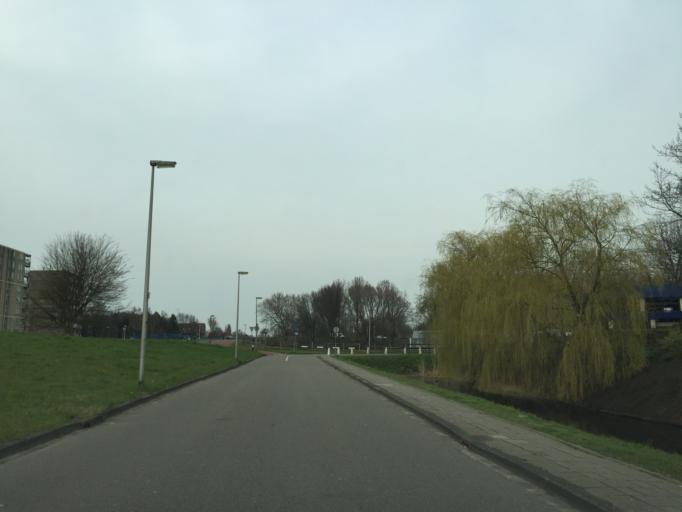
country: NL
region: South Holland
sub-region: Gemeente Zoetermeer
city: Zoetermeer
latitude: 52.0618
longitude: 4.4995
